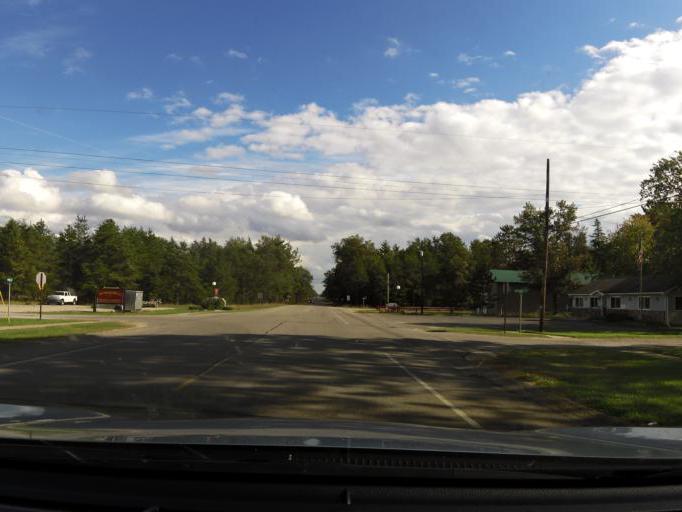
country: US
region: Michigan
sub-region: Roscommon County
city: Roscommon
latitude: 44.4925
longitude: -84.5823
